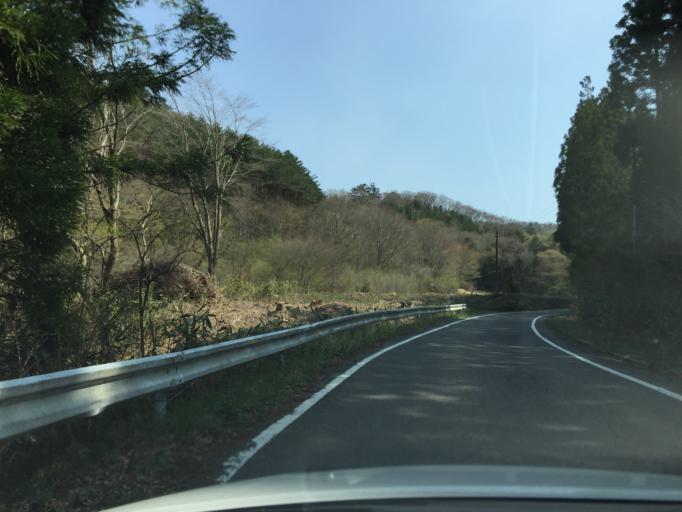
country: JP
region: Fukushima
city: Iwaki
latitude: 37.2316
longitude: 140.8457
